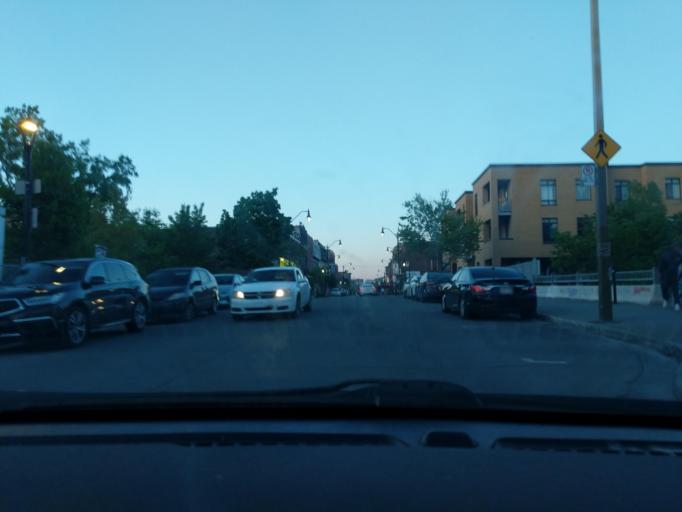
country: CA
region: Quebec
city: Westmount
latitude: 45.4782
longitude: -73.5836
